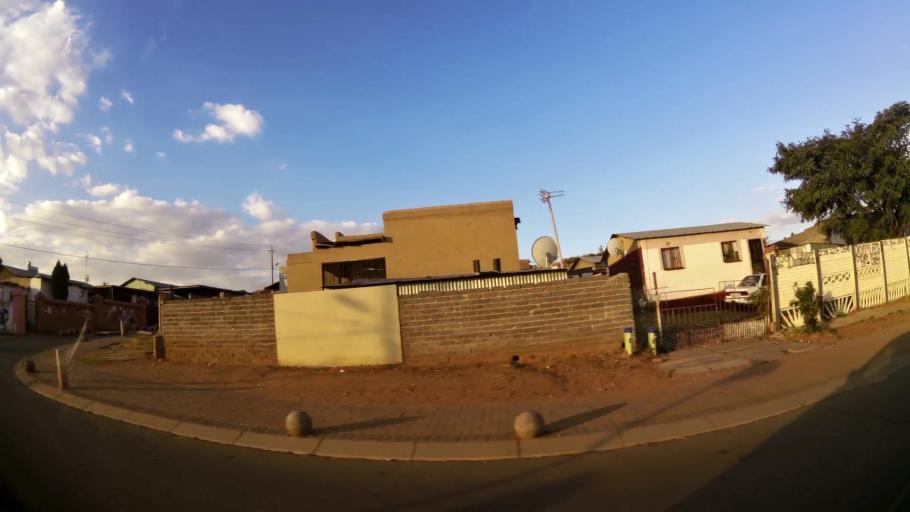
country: ZA
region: Gauteng
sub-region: West Rand District Municipality
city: Krugersdorp
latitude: -26.0797
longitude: 27.7478
